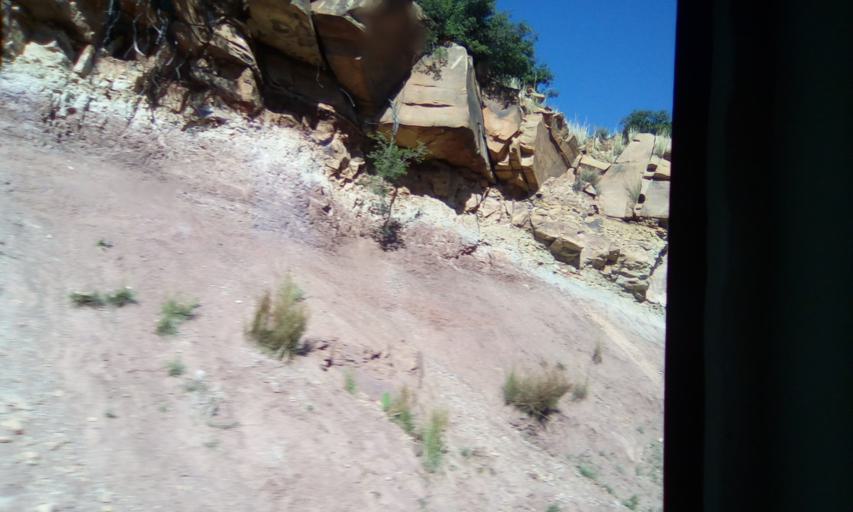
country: LS
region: Qacha's Nek
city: Qacha's Nek
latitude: -30.0454
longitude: 28.3541
